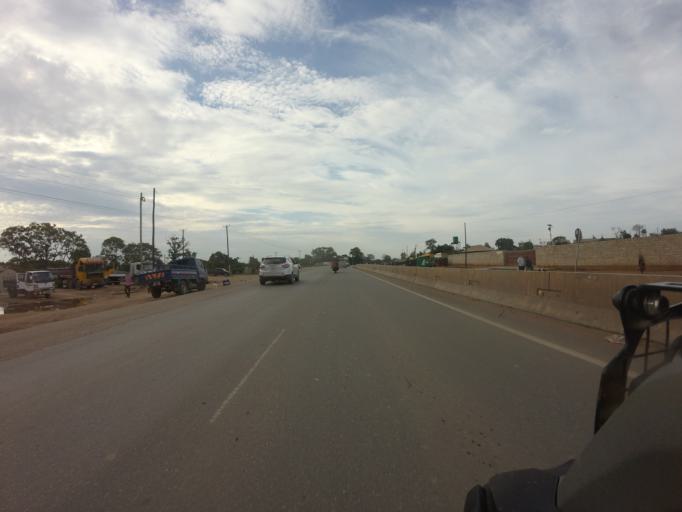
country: ZM
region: Lusaka
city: Lusaka
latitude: -15.5440
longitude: 28.2650
